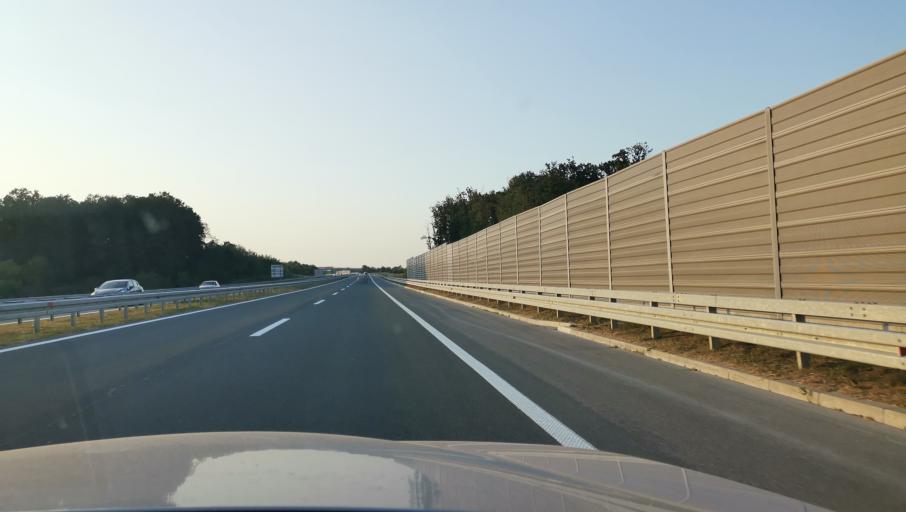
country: RS
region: Central Serbia
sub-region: Kolubarski Okrug
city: Lajkovac
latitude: 44.3715
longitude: 20.1187
